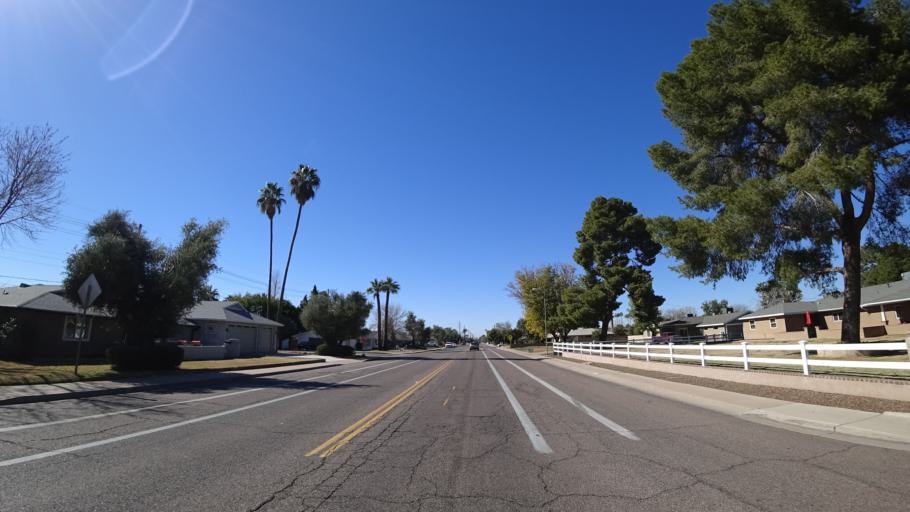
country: US
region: Arizona
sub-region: Maricopa County
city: Paradise Valley
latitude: 33.4875
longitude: -111.9795
